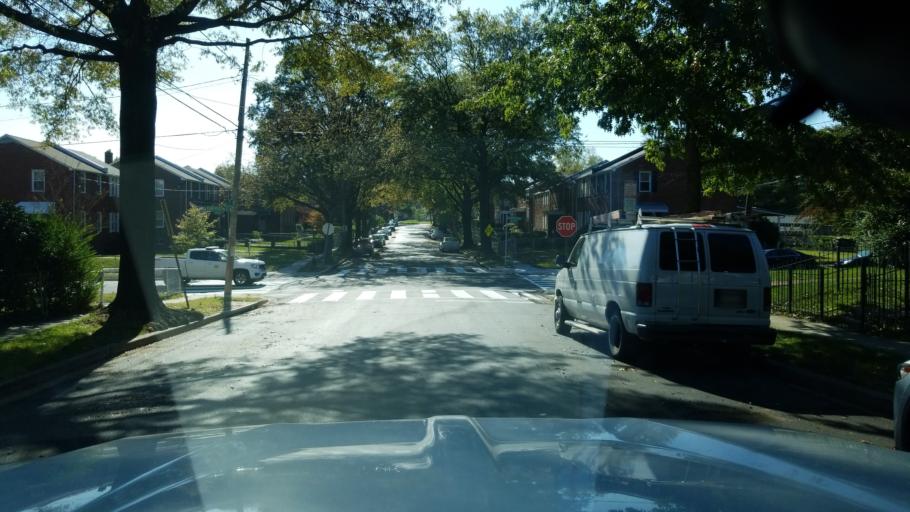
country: US
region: Maryland
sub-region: Prince George's County
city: Chillum
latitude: 38.9506
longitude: -76.9917
